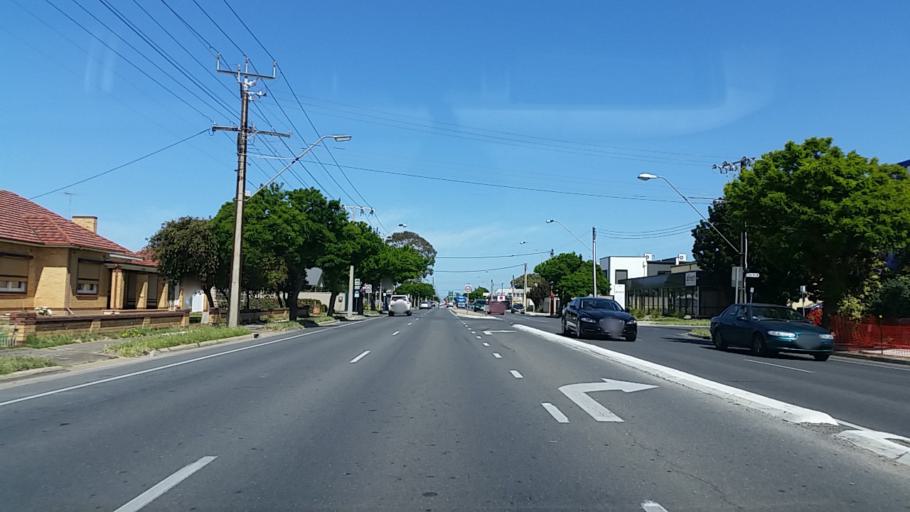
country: AU
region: South Australia
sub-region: Charles Sturt
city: Allenby Gardens
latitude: -34.9042
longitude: 138.5568
